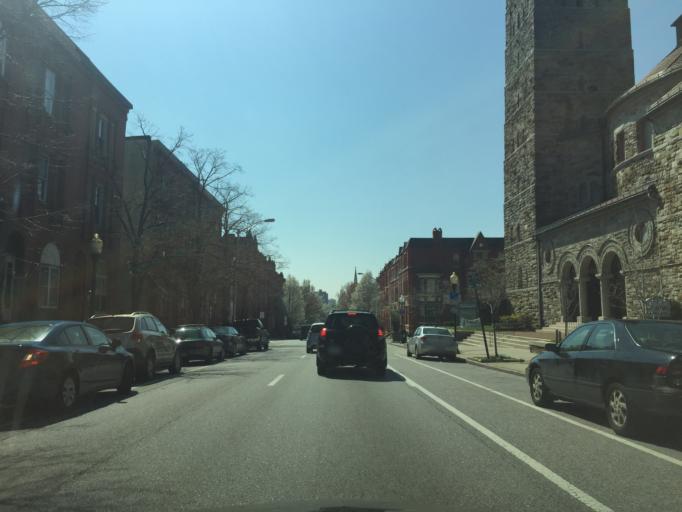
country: US
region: Maryland
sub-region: City of Baltimore
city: Baltimore
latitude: 39.3150
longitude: -76.6152
